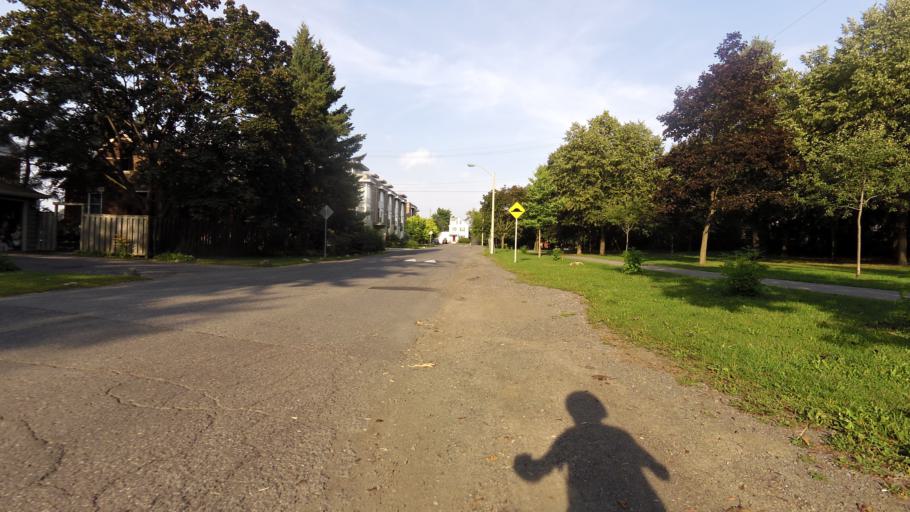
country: CA
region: Ontario
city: Ottawa
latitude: 45.3953
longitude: -75.7404
